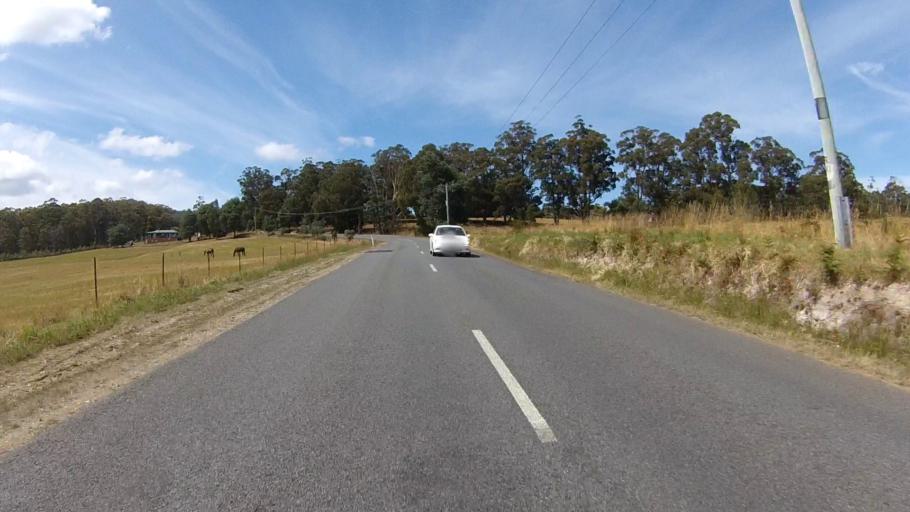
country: AU
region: Tasmania
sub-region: Huon Valley
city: Cygnet
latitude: -43.2127
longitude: 147.1169
